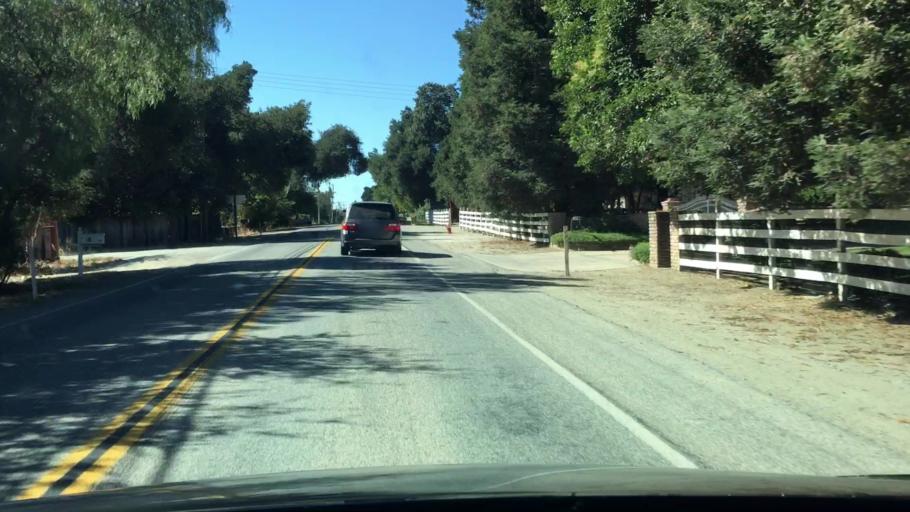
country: US
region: California
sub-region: Santa Clara County
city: Gilroy
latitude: 37.0379
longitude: -121.5398
